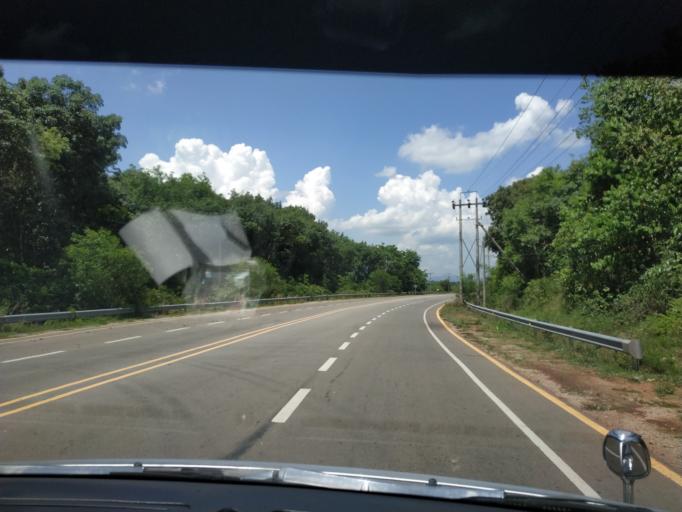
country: MM
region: Mon
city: Kyaikto
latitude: 17.3297
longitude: 97.0269
